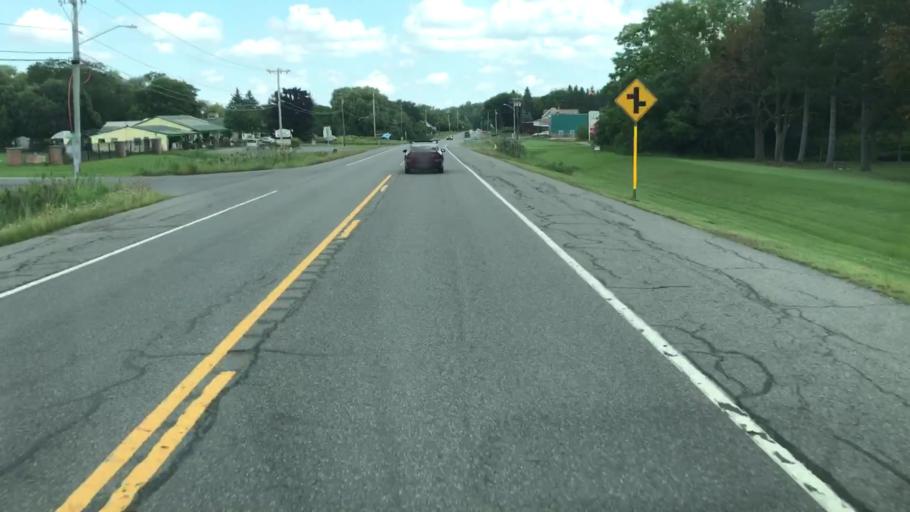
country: US
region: New York
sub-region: Onondaga County
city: Westvale
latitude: 42.9975
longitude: -76.2053
